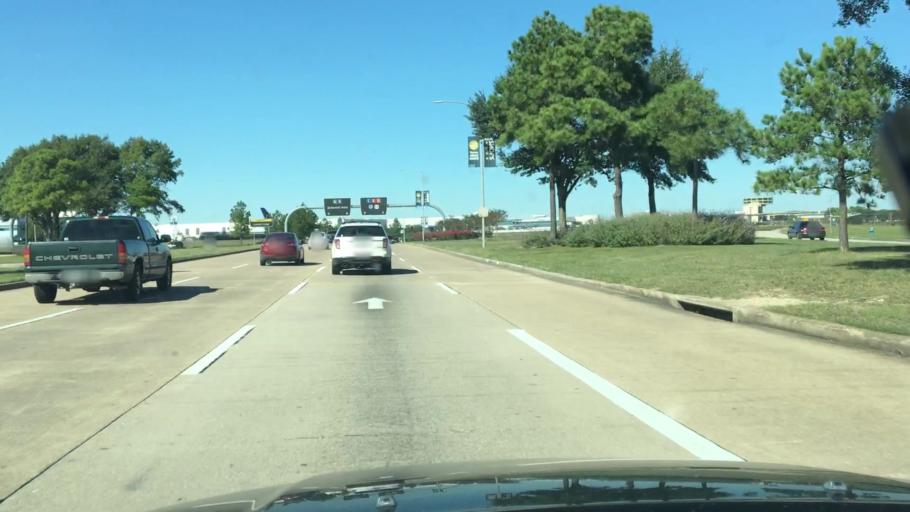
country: US
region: Texas
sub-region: Harris County
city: Aldine
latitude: 29.9742
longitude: -95.3412
